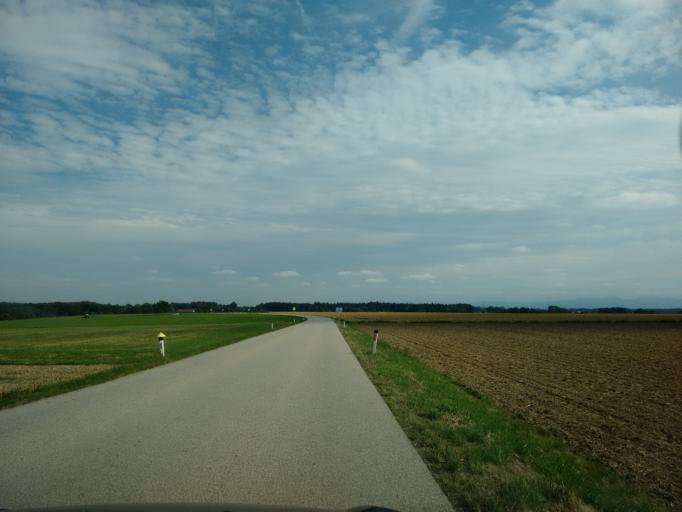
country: AT
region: Upper Austria
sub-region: Wels-Land
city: Marchtrenk
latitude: 48.1207
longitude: 14.1235
